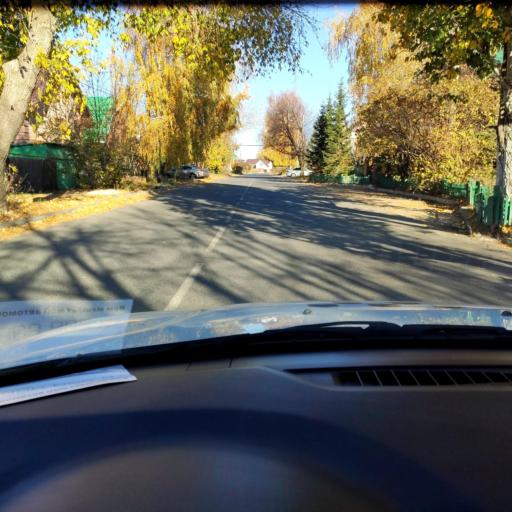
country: RU
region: Samara
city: Tol'yatti
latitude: 53.5257
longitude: 49.4037
